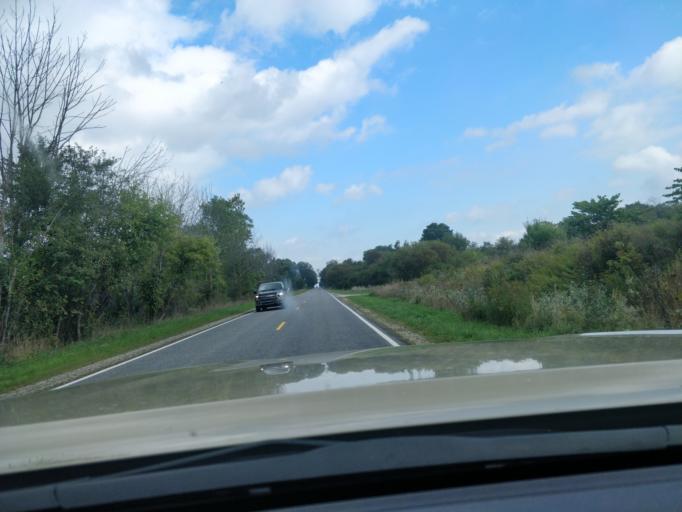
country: US
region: Michigan
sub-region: Ionia County
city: Saranac
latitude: 42.8862
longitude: -85.2552
